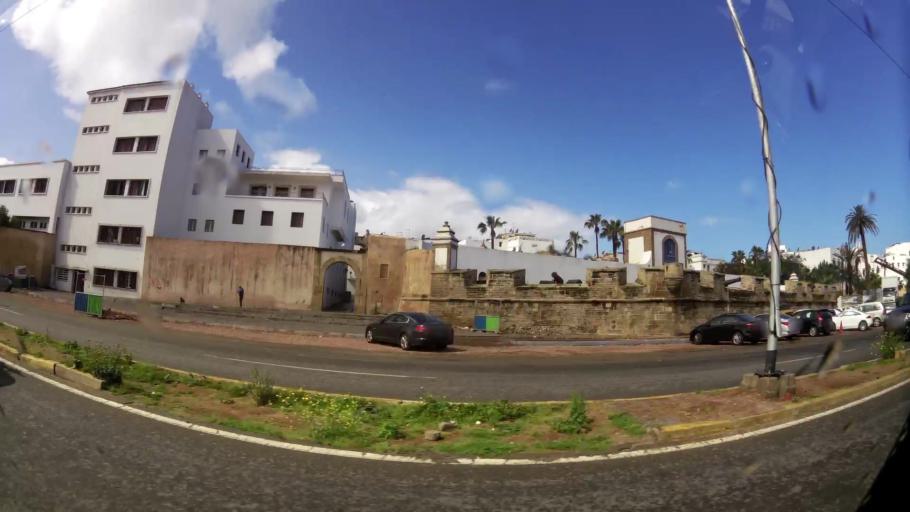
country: MA
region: Grand Casablanca
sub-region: Casablanca
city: Casablanca
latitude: 33.6029
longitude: -7.6187
